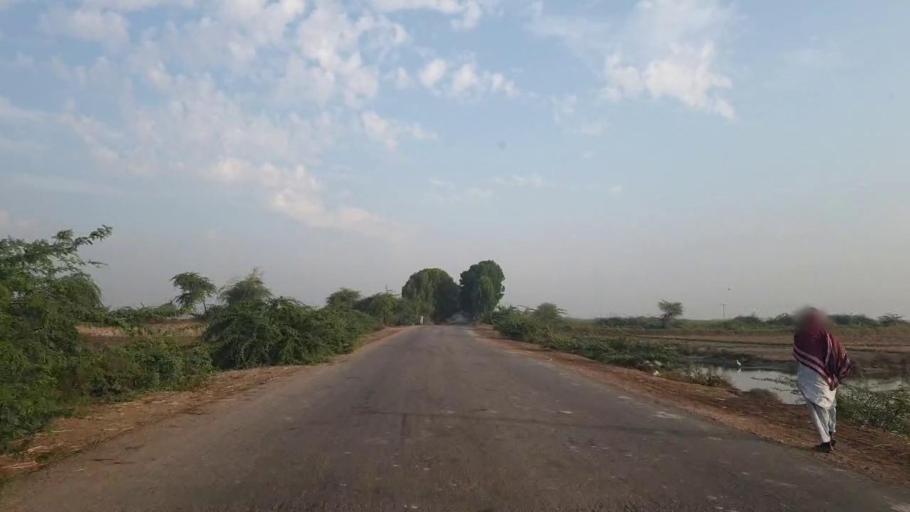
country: PK
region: Sindh
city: Tando Bago
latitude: 24.7258
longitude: 68.9426
